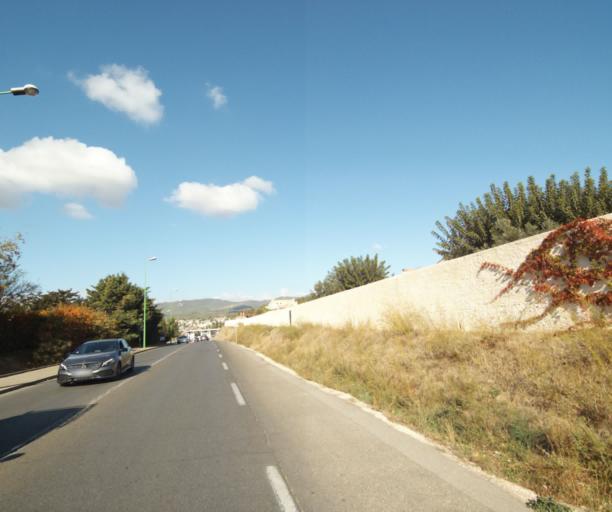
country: FR
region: Provence-Alpes-Cote d'Azur
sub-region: Departement des Bouches-du-Rhone
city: Allauch
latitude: 43.3400
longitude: 5.4735
